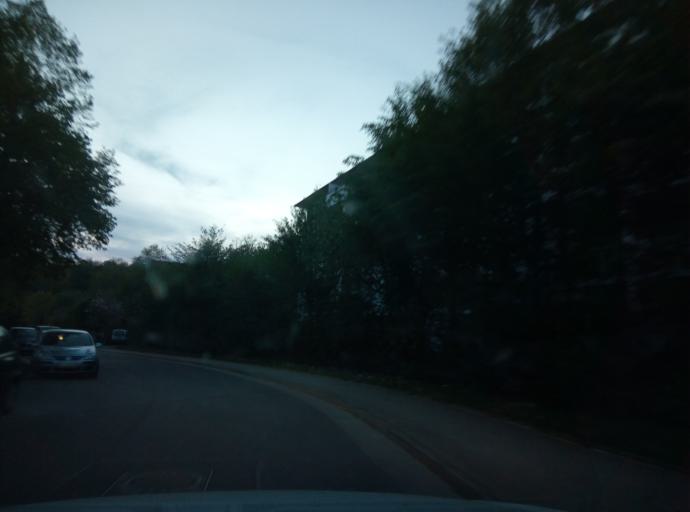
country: DE
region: Baden-Wuerttemberg
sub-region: Tuebingen Region
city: Kusterdingen
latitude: 48.5363
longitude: 9.0922
